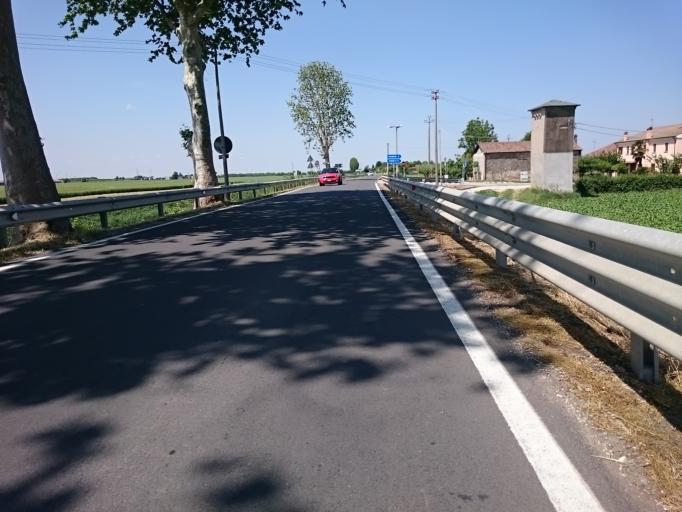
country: IT
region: Veneto
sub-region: Provincia di Padova
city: Lozzo Atestino
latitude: 45.2634
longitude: 11.6174
